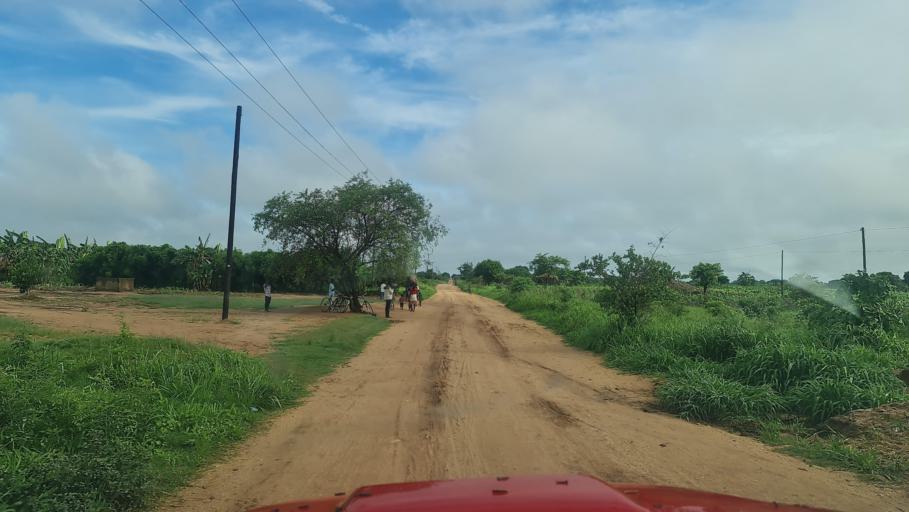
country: MW
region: Southern Region
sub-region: Nsanje District
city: Nsanje
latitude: -17.3137
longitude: 35.5925
